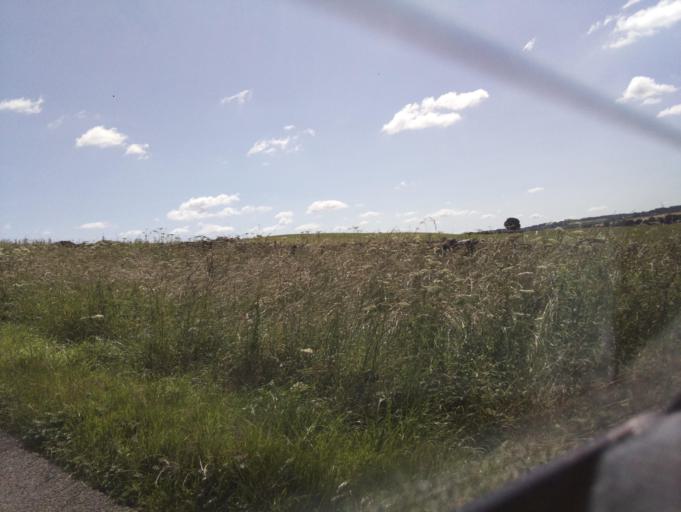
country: GB
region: England
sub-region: Derbyshire
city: Tideswell
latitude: 53.1981
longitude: -1.7559
